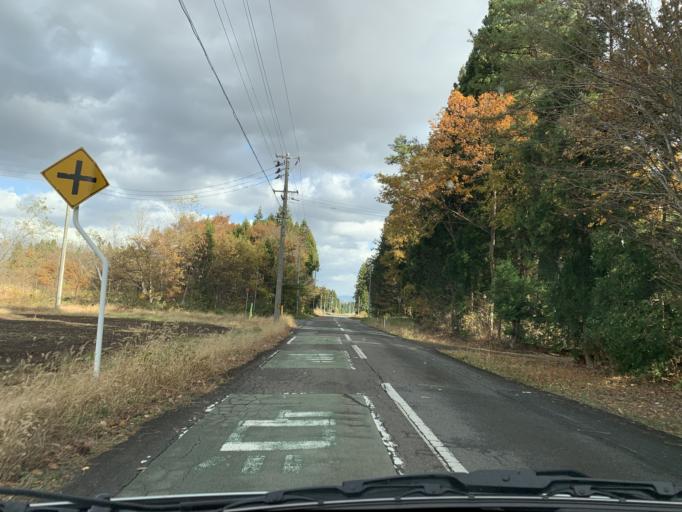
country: JP
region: Iwate
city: Mizusawa
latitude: 39.1163
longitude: 140.9988
